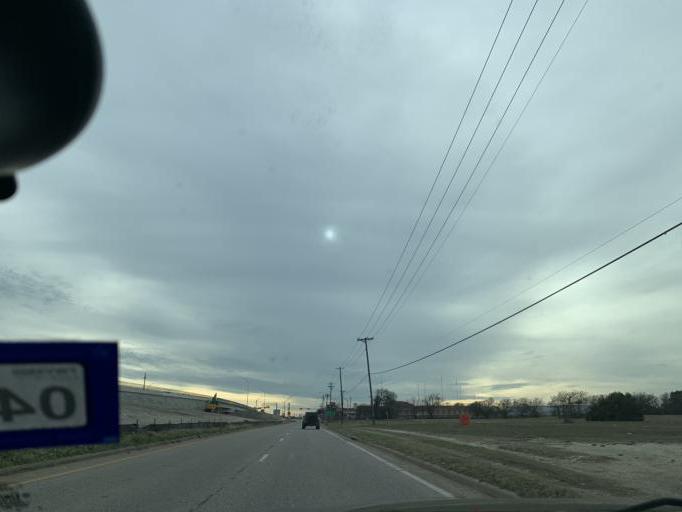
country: US
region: Texas
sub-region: Dallas County
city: Duncanville
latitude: 32.6206
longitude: -96.9139
